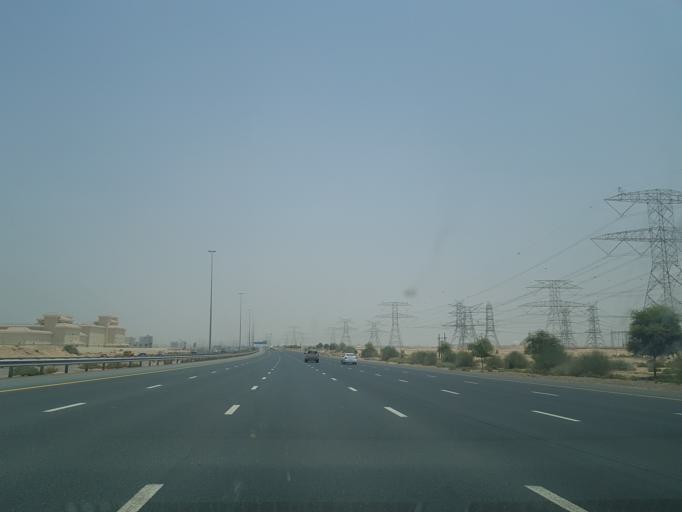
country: AE
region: Dubai
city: Dubai
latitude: 25.0724
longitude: 55.3682
